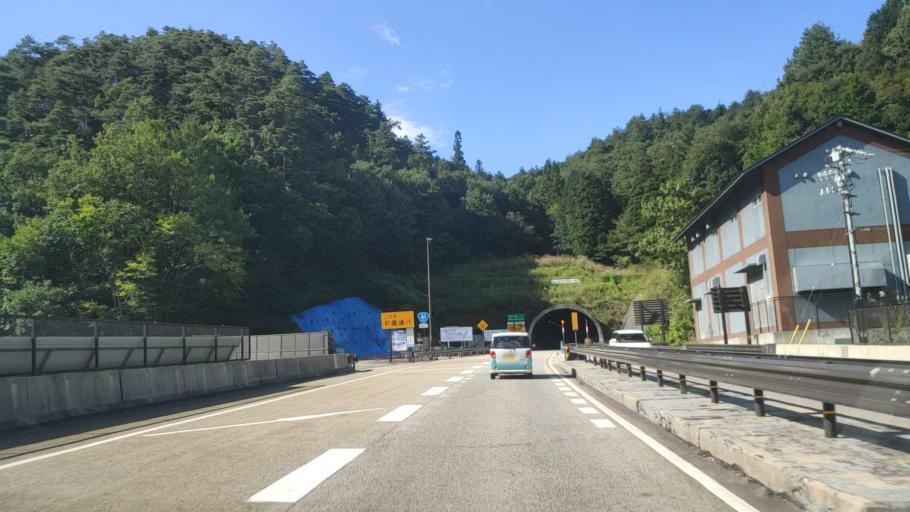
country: JP
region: Gifu
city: Takayama
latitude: 36.1709
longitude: 137.2257
